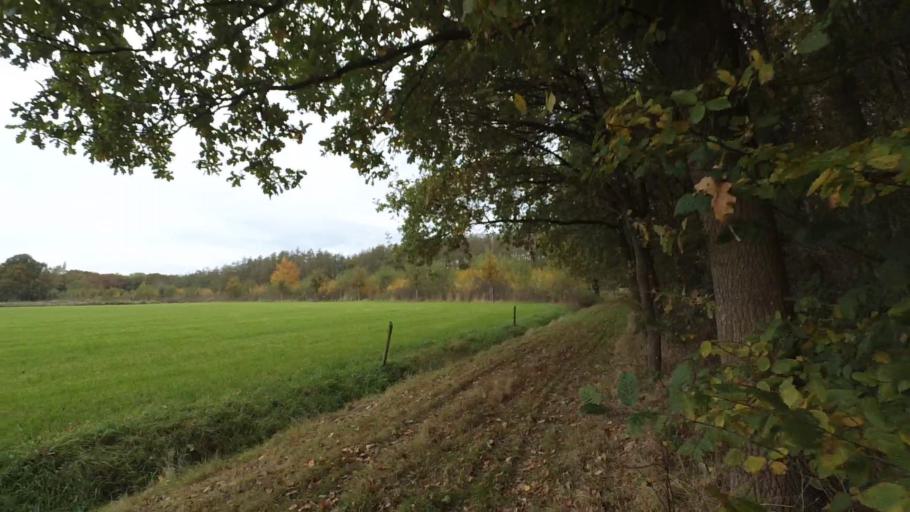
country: NL
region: Gelderland
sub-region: Gemeente Barneveld
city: Terschuur
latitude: 52.1450
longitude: 5.5201
